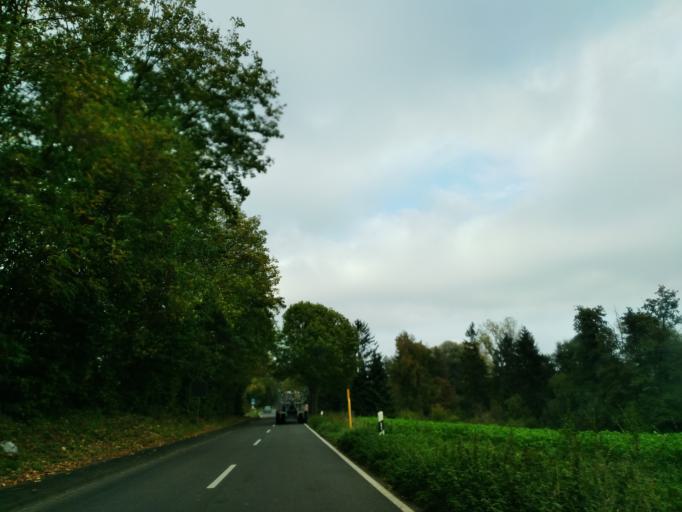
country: DE
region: North Rhine-Westphalia
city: Sankt Augustin
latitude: 50.7338
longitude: 7.2193
